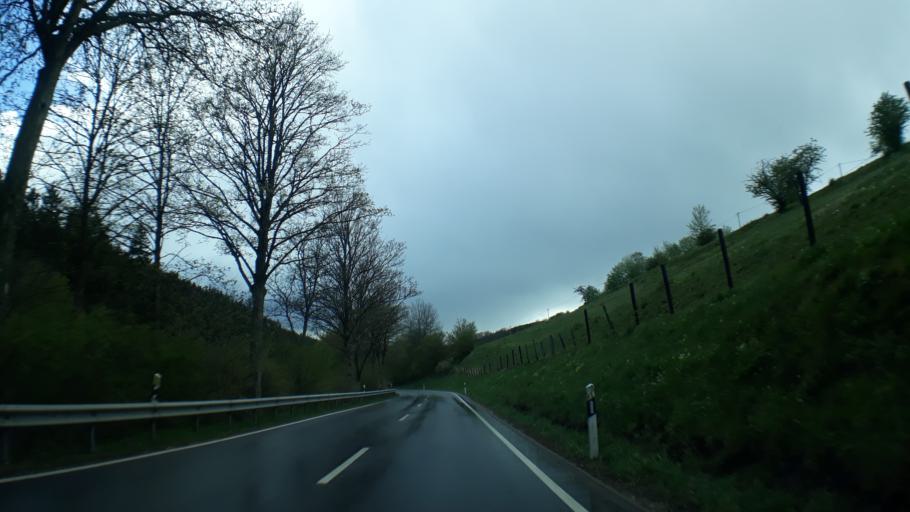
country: DE
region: North Rhine-Westphalia
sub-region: Regierungsbezirk Koln
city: Schleiden
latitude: 50.4830
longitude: 6.4870
